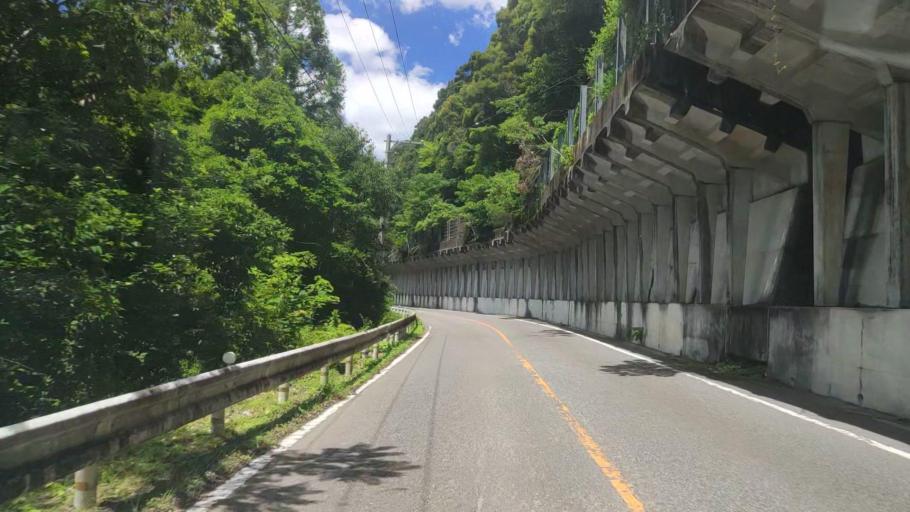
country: JP
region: Mie
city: Owase
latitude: 33.9996
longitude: 136.0104
